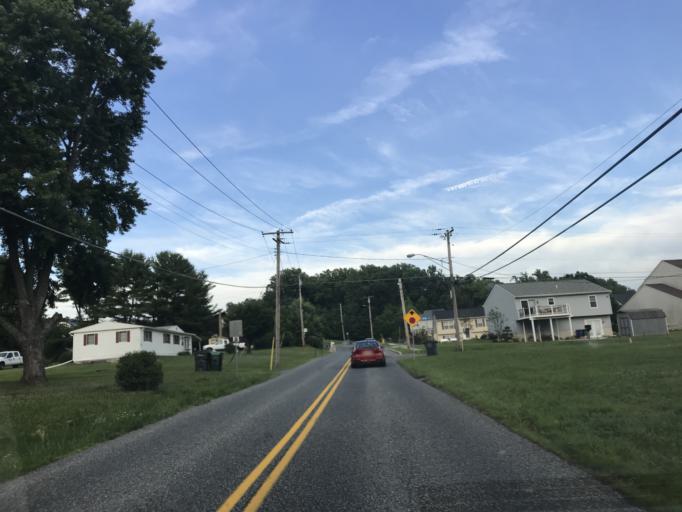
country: US
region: Maryland
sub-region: Harford County
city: Aberdeen
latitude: 39.5154
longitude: -76.1902
